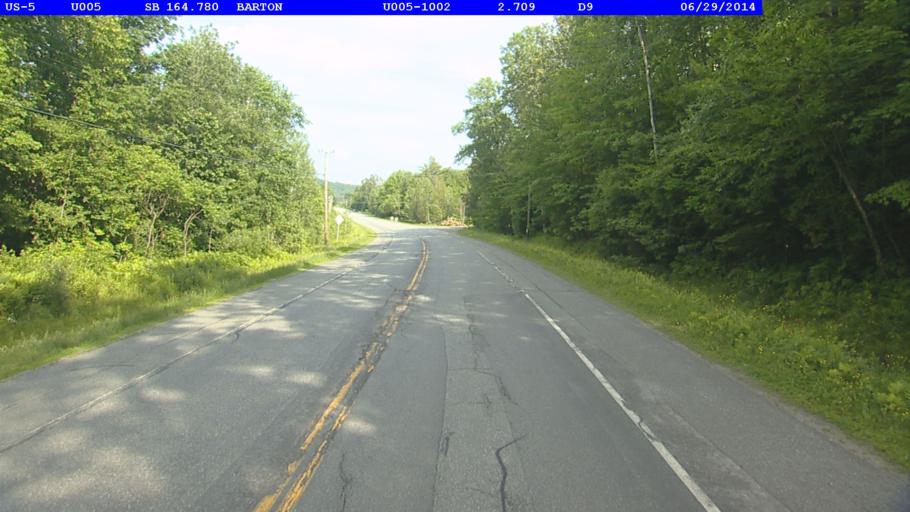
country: US
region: Vermont
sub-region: Orleans County
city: Newport
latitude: 44.7175
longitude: -72.1434
